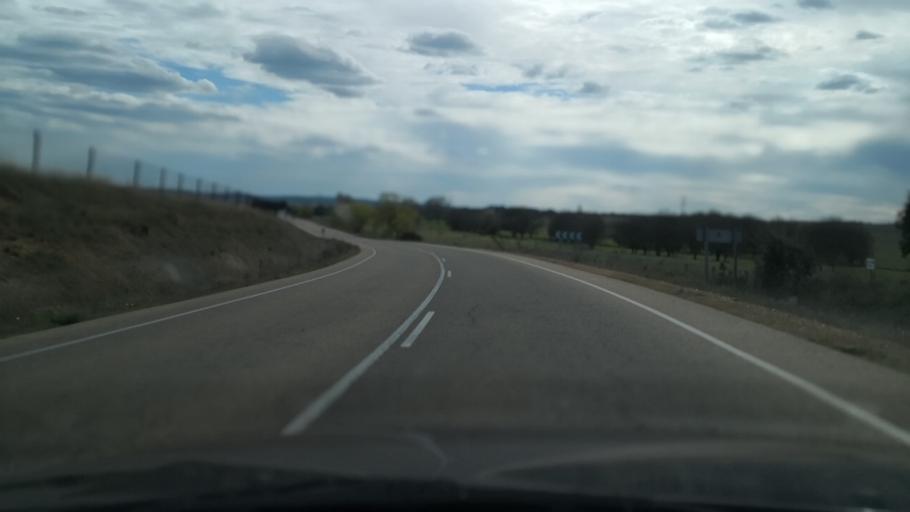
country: ES
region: Castille and Leon
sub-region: Provincia de Salamanca
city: Ciudad Rodrigo
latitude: 40.5641
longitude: -6.5515
